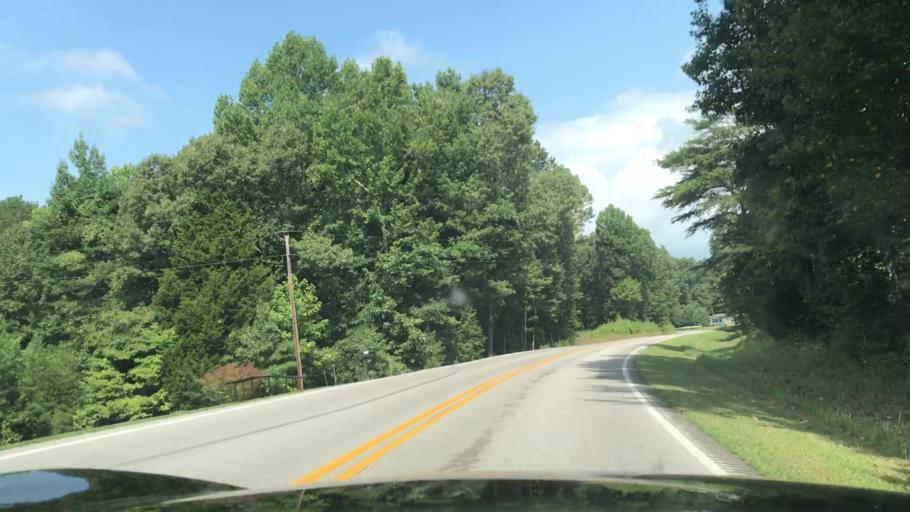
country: US
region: Kentucky
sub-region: Butler County
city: Morgantown
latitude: 37.1829
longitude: -86.8715
